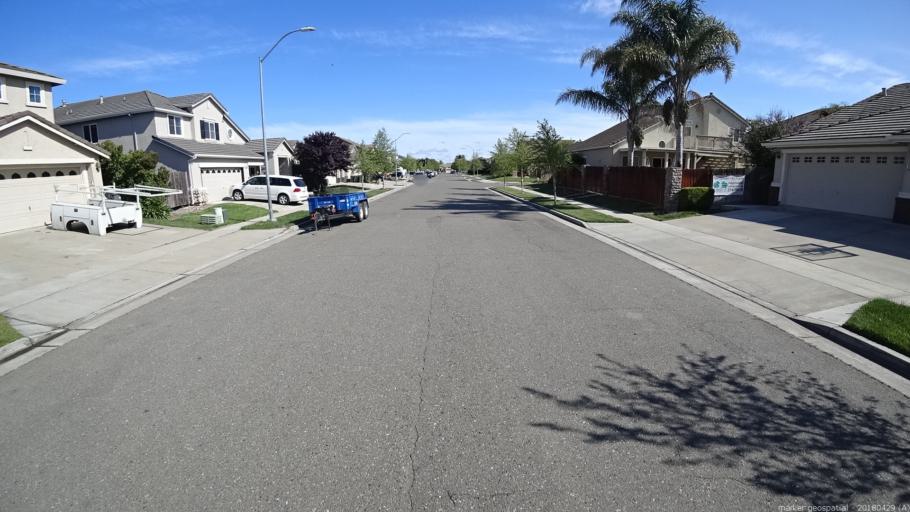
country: US
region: California
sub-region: Yolo County
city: West Sacramento
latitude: 38.5364
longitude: -121.5811
